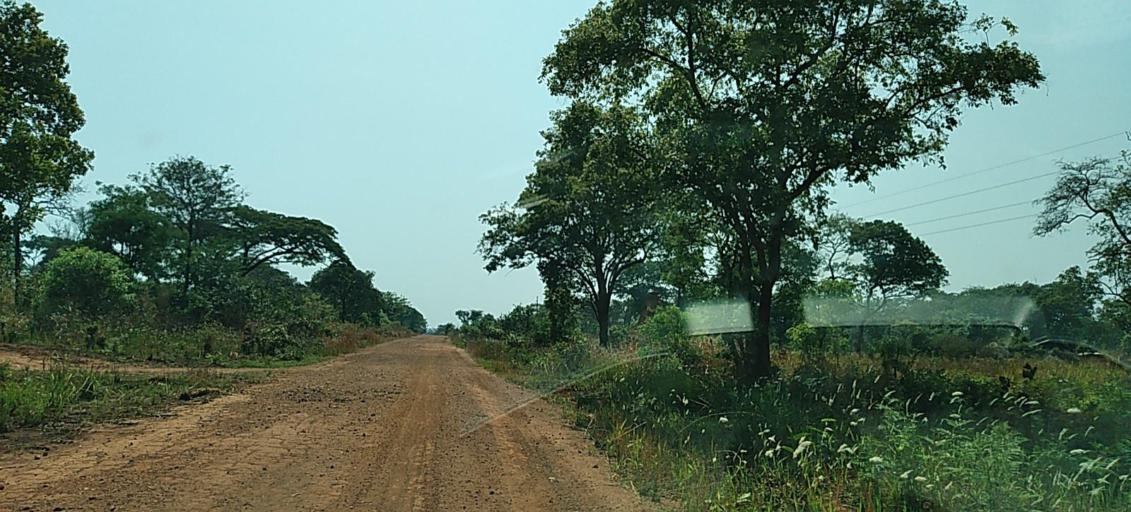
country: ZM
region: North-Western
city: Kansanshi
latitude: -12.0070
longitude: 26.5237
